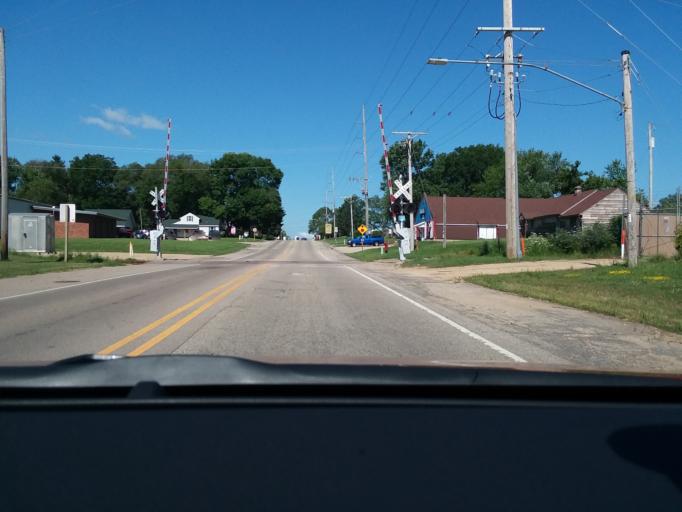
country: US
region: Wisconsin
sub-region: Dane County
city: De Forest
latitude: 43.2527
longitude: -89.3410
